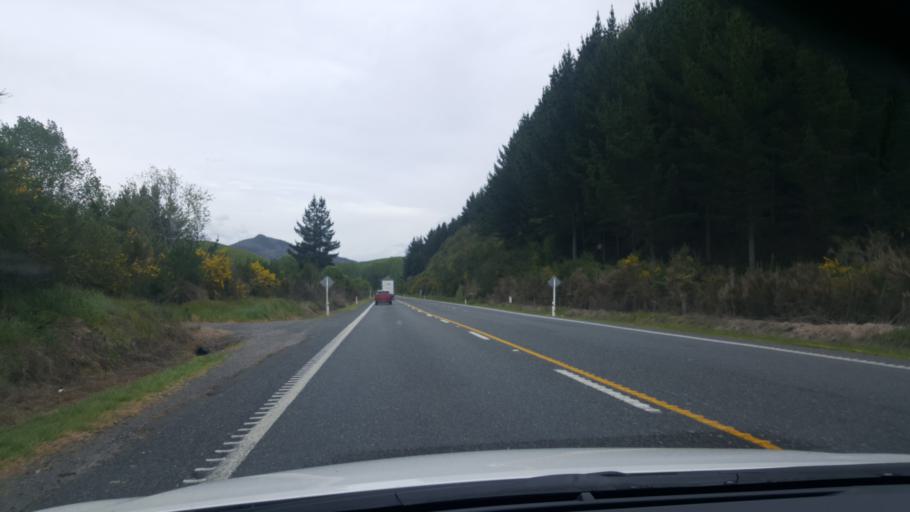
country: NZ
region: Bay of Plenty
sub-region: Rotorua District
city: Rotorua
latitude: -38.2902
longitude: 176.3524
